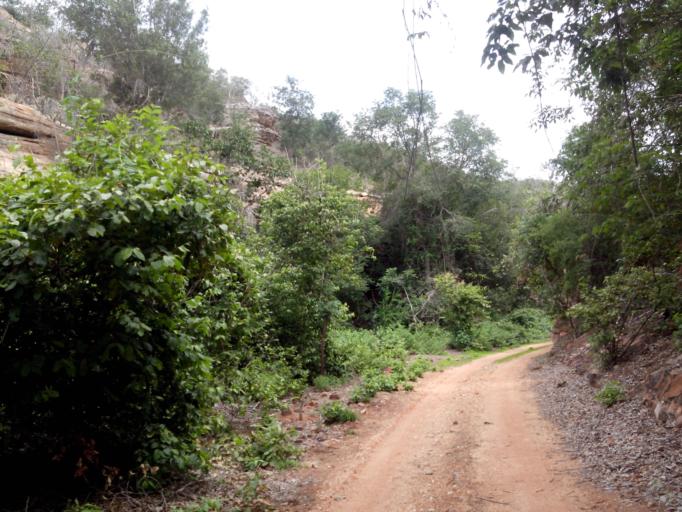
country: BR
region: Piaui
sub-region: Sao Raimundo Nonato
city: Sao Raimundo Nonato
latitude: -8.7729
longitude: -42.4817
